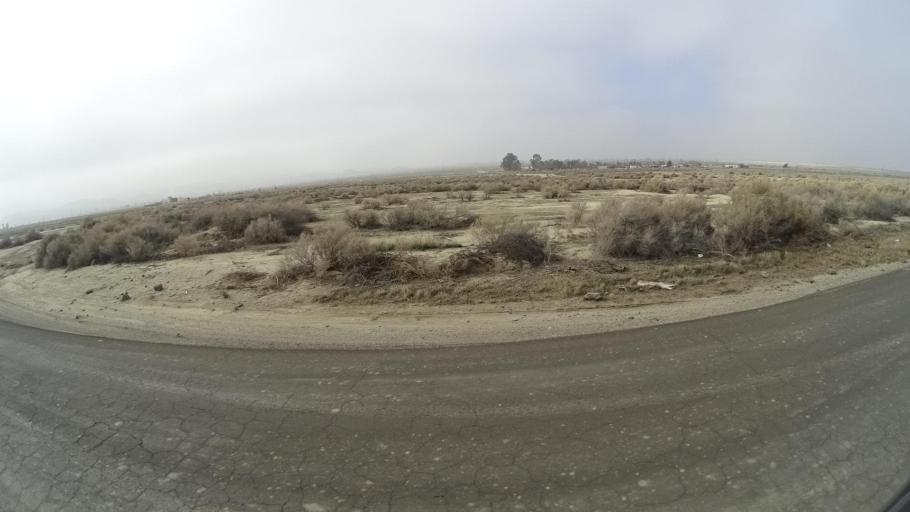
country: US
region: California
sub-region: Kern County
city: Maricopa
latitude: 35.0538
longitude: -119.3671
